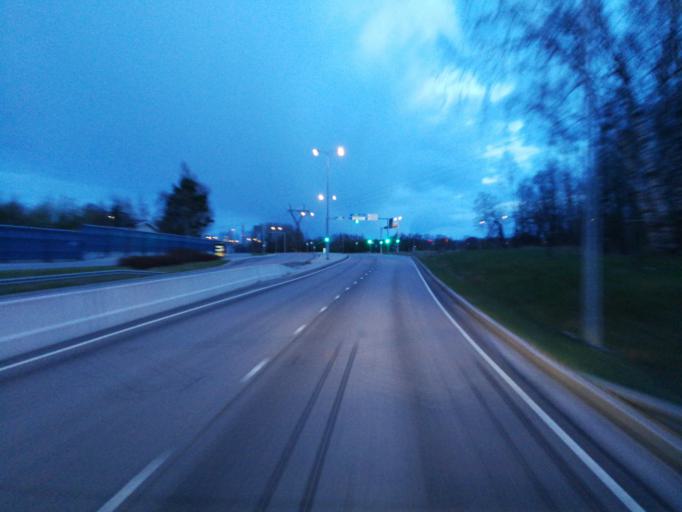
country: FI
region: Varsinais-Suomi
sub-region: Turku
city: Raisio
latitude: 60.4582
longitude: 22.1948
